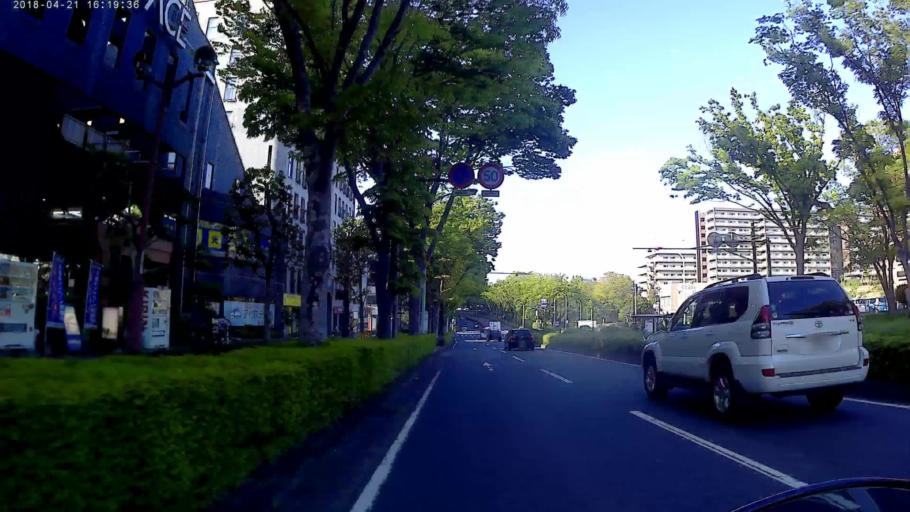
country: JP
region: Kanagawa
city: Fujisawa
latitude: 35.3654
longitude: 139.4462
